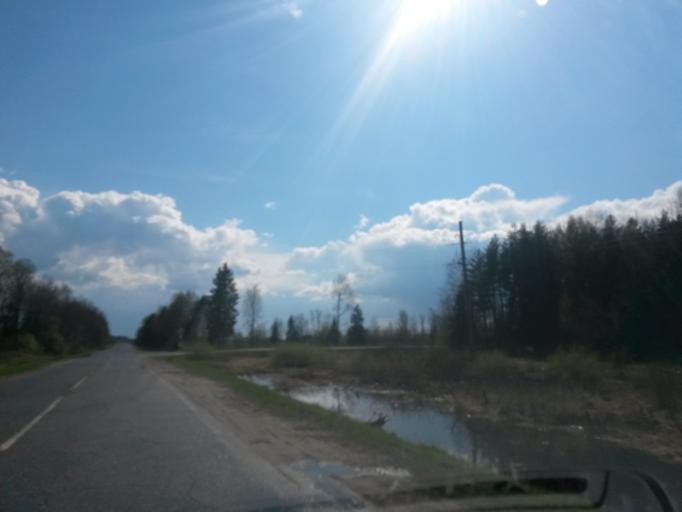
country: RU
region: Jaroslavl
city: Tutayev
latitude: 57.9500
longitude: 39.4989
